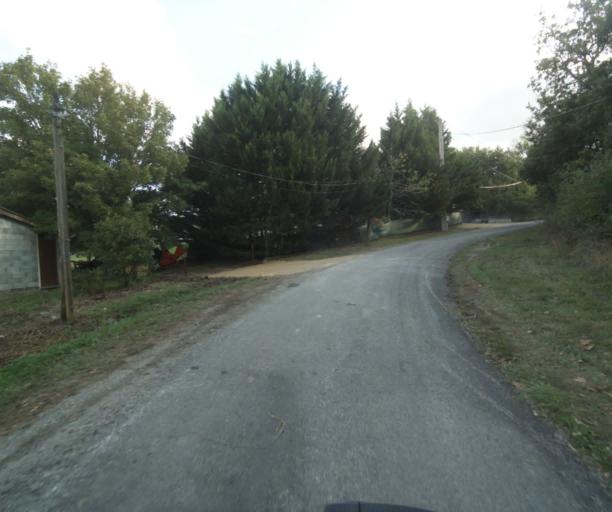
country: FR
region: Midi-Pyrenees
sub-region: Departement de la Haute-Garonne
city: Launac
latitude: 43.8141
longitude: 1.1326
